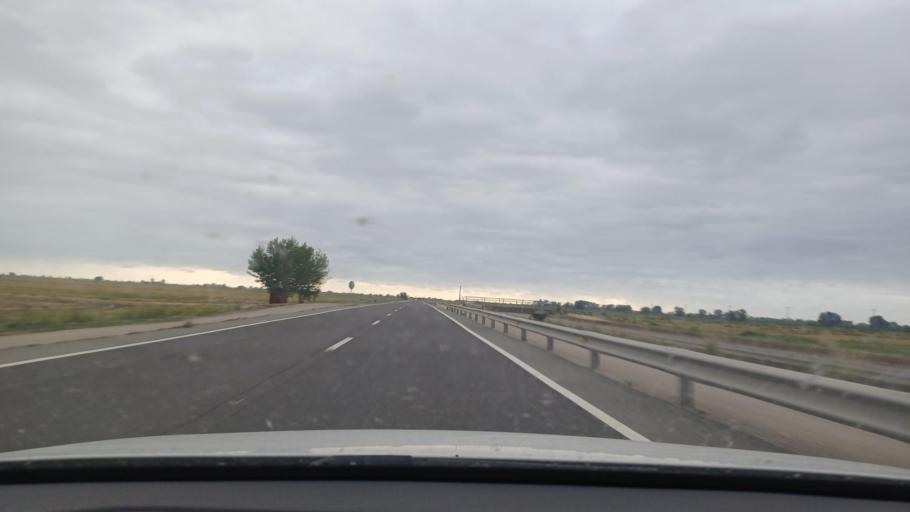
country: ES
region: Catalonia
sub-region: Provincia de Tarragona
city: Amposta
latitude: 40.7128
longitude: 0.5993
